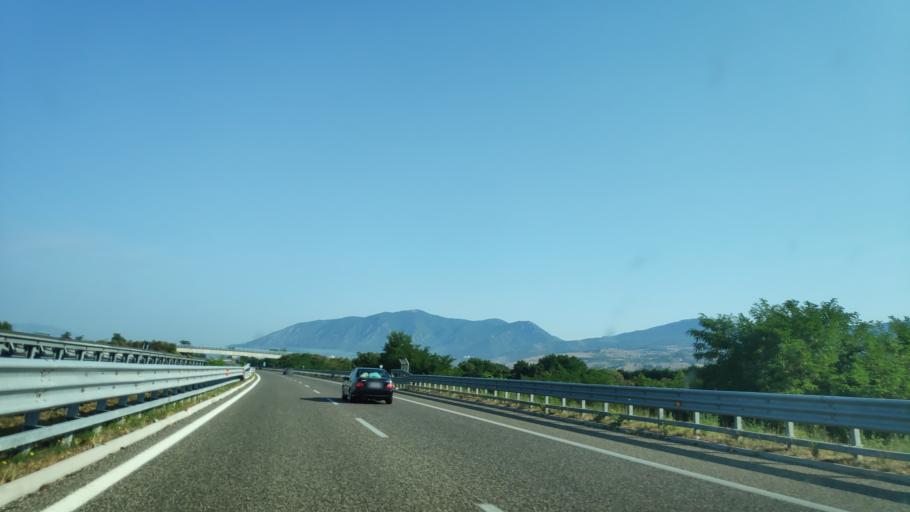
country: IT
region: Campania
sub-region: Provincia di Salerno
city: Padula
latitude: 40.3229
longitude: 15.6375
